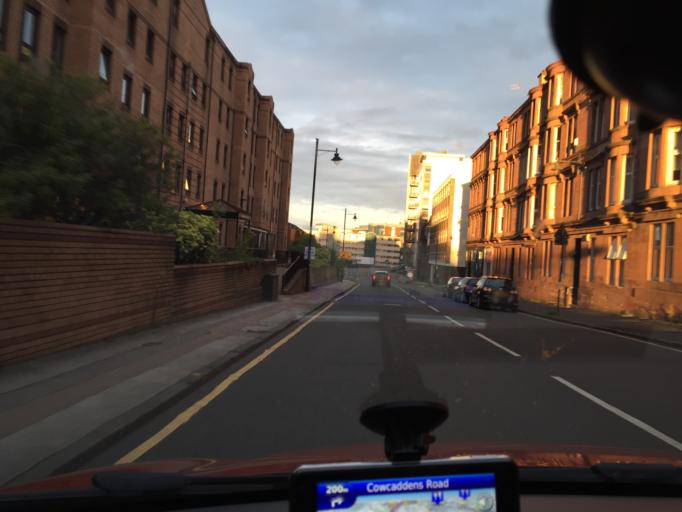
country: GB
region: Scotland
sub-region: Glasgow City
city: Glasgow
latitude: 55.8684
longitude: -4.2635
